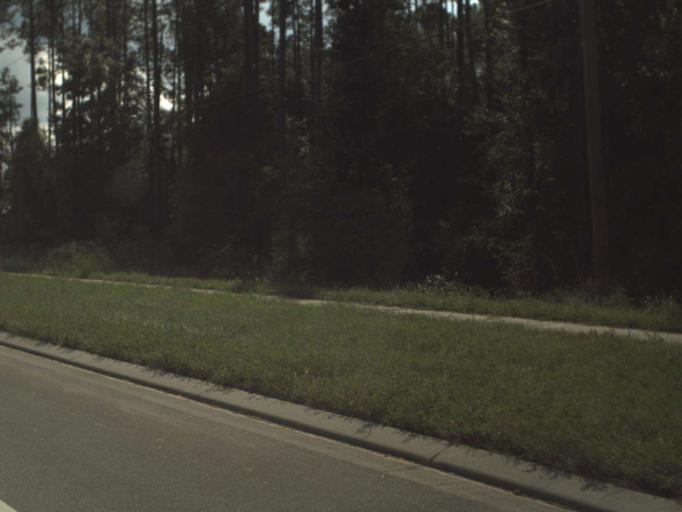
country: US
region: Florida
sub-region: Bay County
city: Laguna Beach
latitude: 30.4334
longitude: -85.8744
